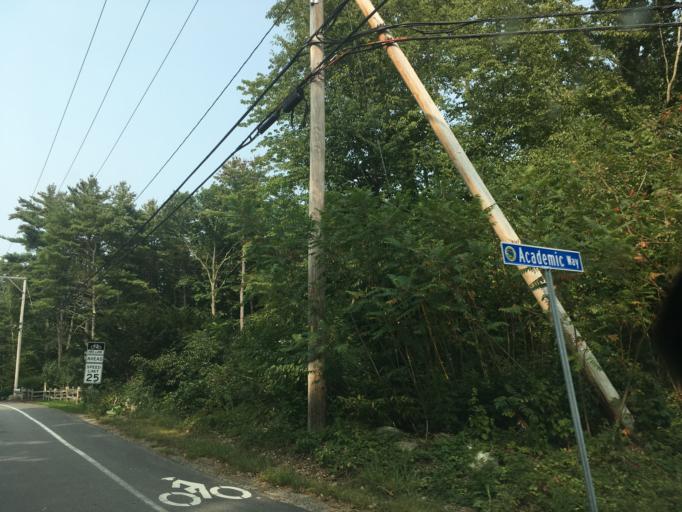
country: US
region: New Hampshire
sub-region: Rockingham County
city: Exeter
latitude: 42.9806
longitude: -70.9066
